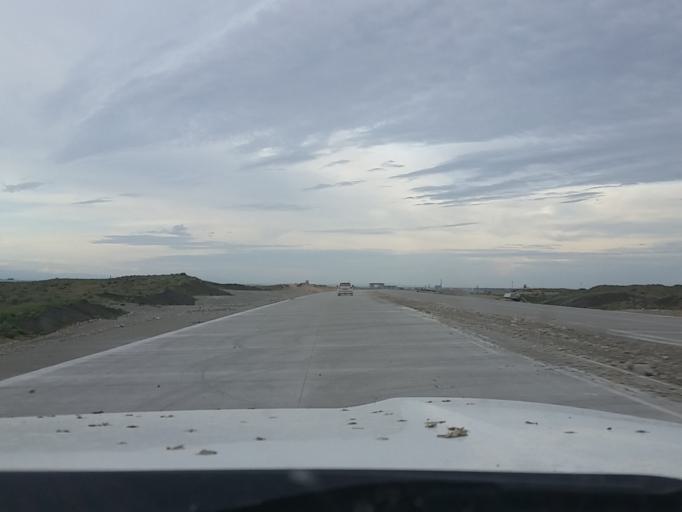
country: KZ
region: Almaty Oblysy
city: Zharkent
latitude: 44.1738
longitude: 80.3387
